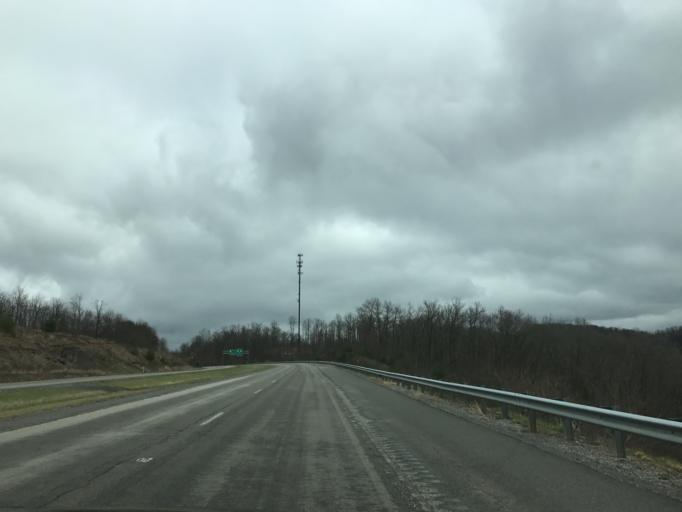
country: US
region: West Virginia
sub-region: Raleigh County
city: Sophia
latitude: 37.7139
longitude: -81.2686
